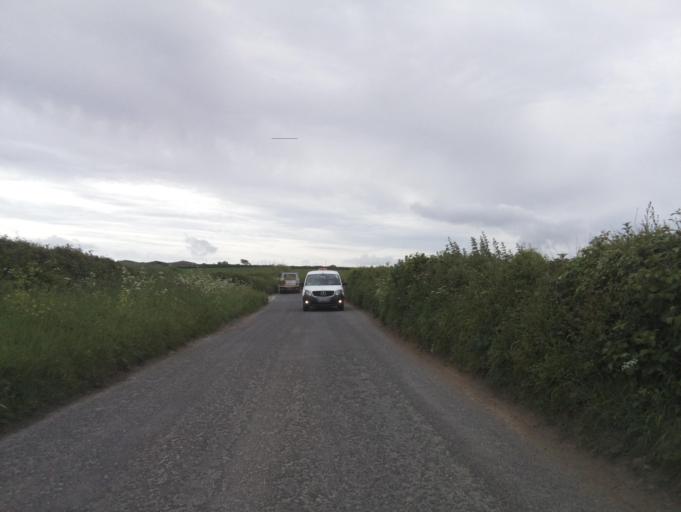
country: GB
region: England
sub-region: Devon
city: Dartmouth
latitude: 50.3240
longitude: -3.6389
